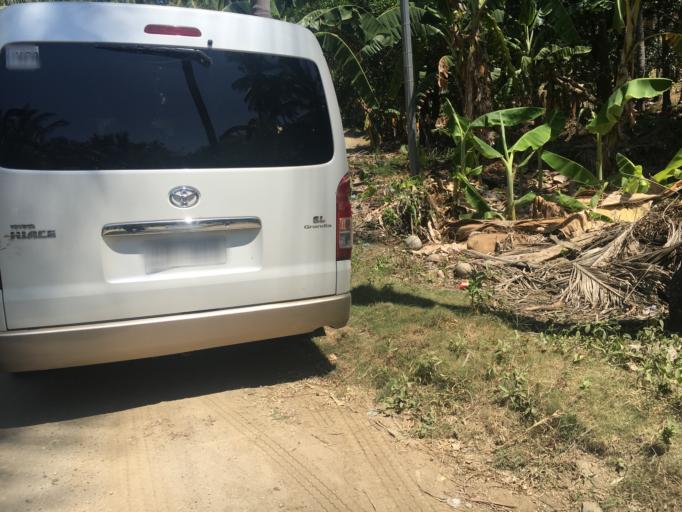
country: PH
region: Davao
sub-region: Province of Davao del Sur
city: Tubalan
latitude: 6.5303
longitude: 125.5605
